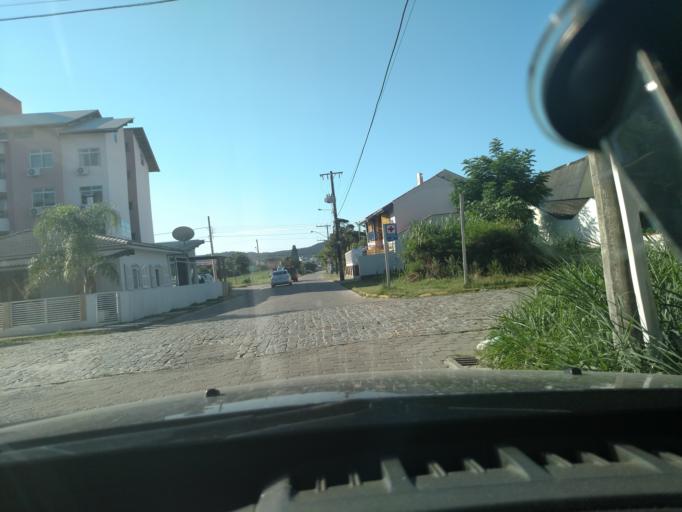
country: BR
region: Santa Catarina
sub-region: Porto Belo
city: Porto Belo
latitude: -27.1956
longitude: -48.4992
